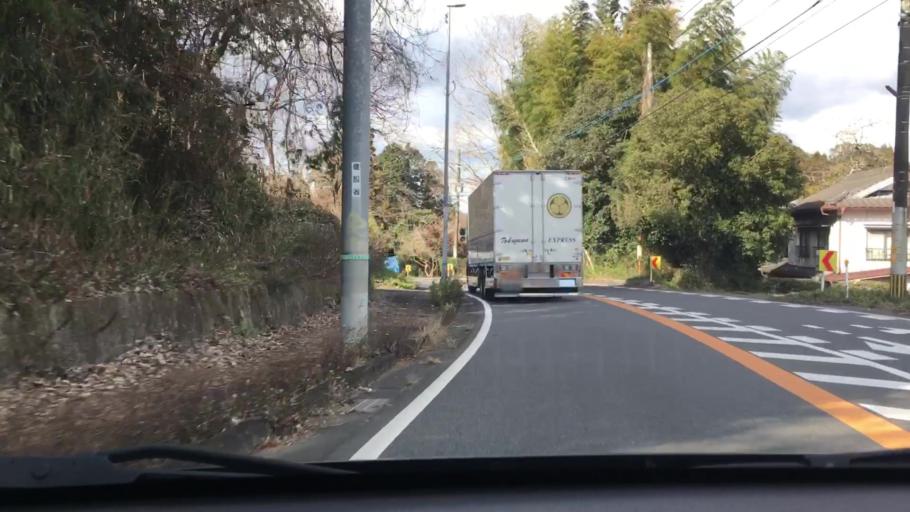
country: JP
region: Oita
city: Usuki
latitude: 33.0300
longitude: 131.6938
